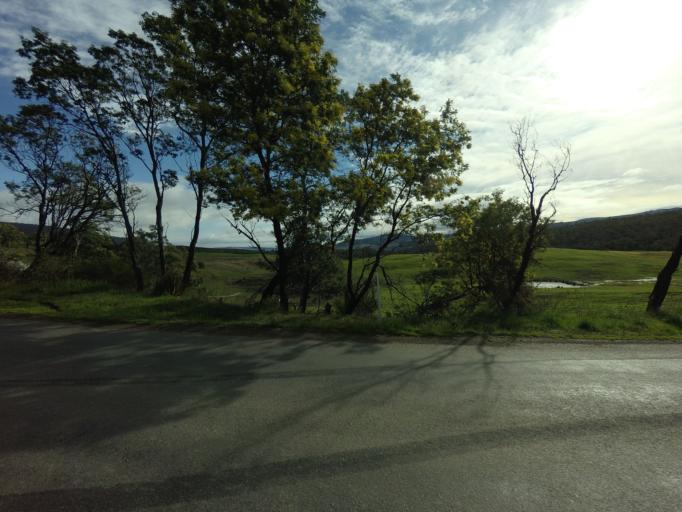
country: AU
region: Tasmania
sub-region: Derwent Valley
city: New Norfolk
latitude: -42.7835
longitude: 146.9961
